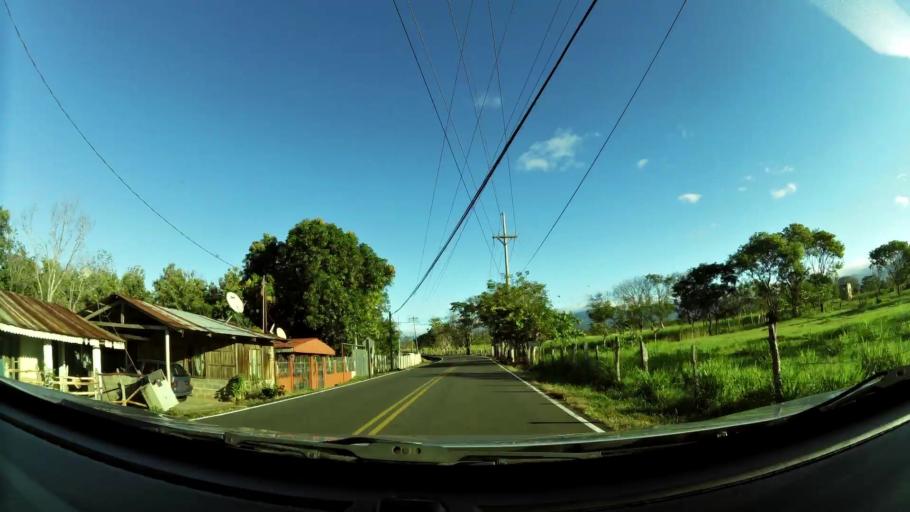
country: CR
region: Puntarenas
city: Miramar
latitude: 10.0960
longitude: -84.8208
